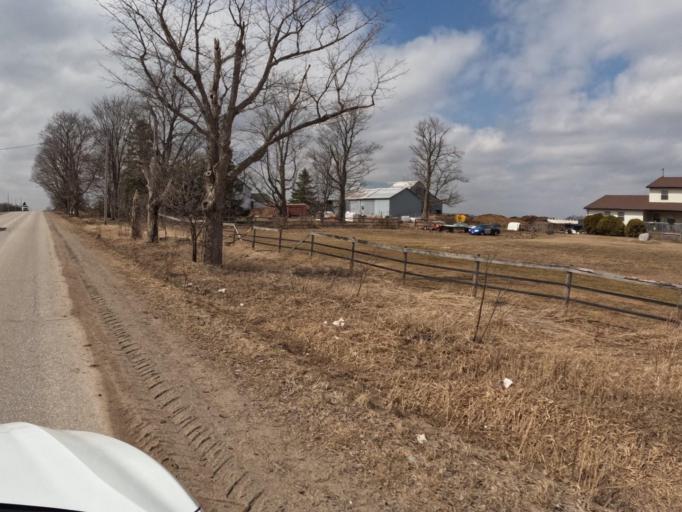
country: CA
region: Ontario
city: Shelburne
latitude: 44.0180
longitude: -80.1678
